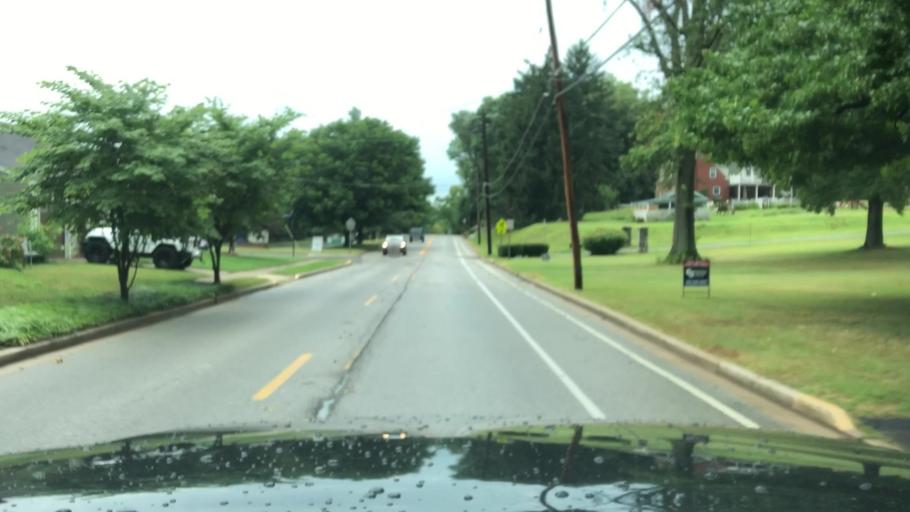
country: US
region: Missouri
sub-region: Saint Charles County
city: Saint Charles
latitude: 38.7896
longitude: -90.4968
